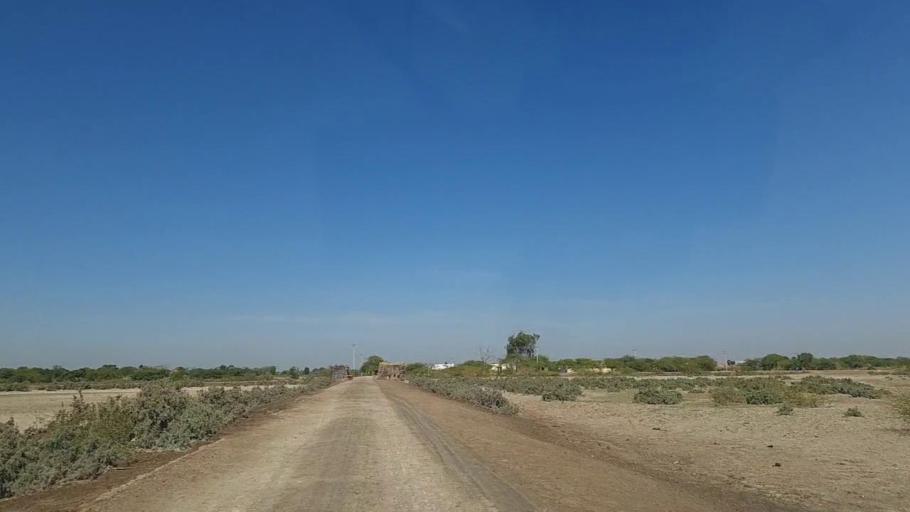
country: PK
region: Sindh
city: Samaro
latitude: 25.3073
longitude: 69.4859
